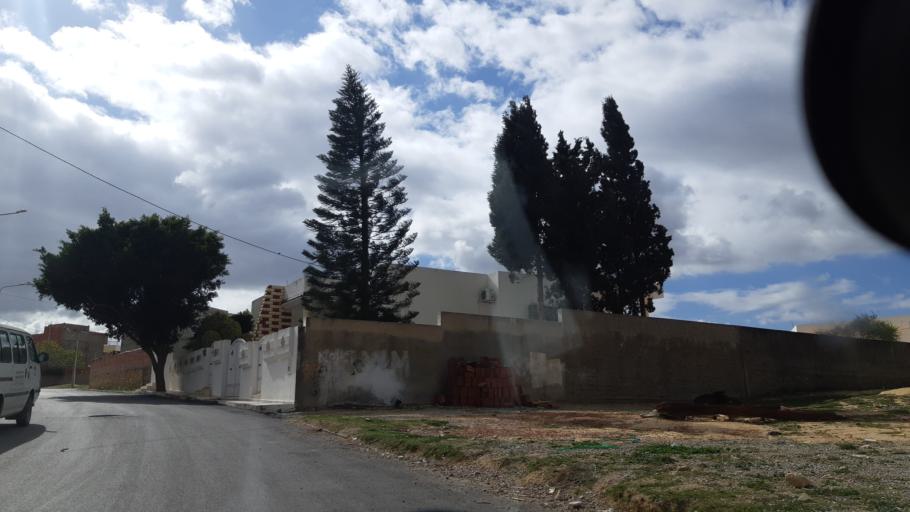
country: TN
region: Susah
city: Akouda
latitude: 35.8729
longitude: 10.5179
